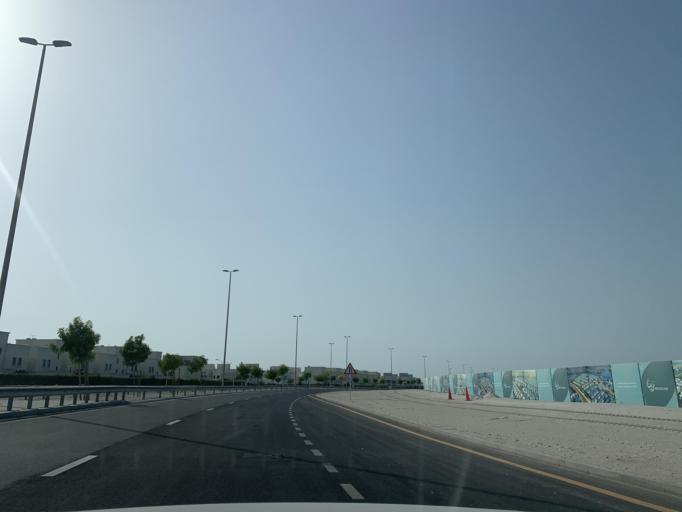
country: BH
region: Muharraq
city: Al Muharraq
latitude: 26.3144
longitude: 50.6330
